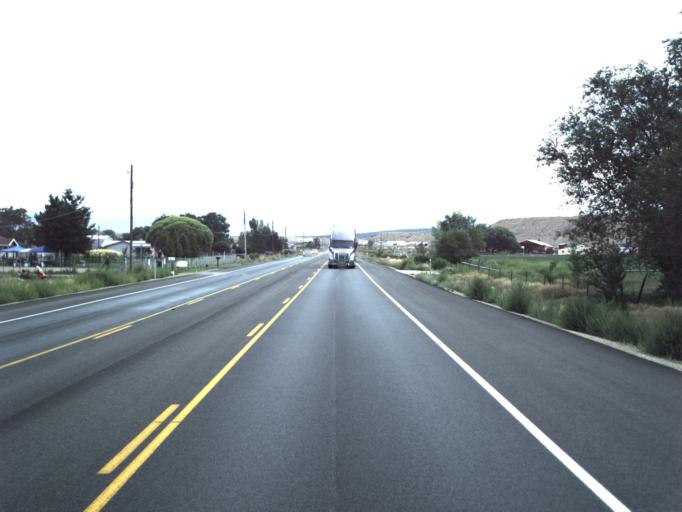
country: US
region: Utah
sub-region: Carbon County
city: Wellington
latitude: 39.5433
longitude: -110.6826
